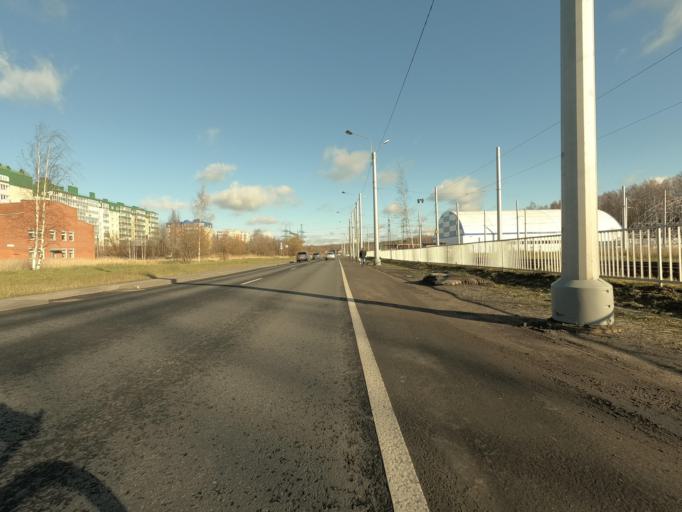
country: RU
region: St.-Petersburg
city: Krasnogvargeisky
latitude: 59.9625
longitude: 30.4919
